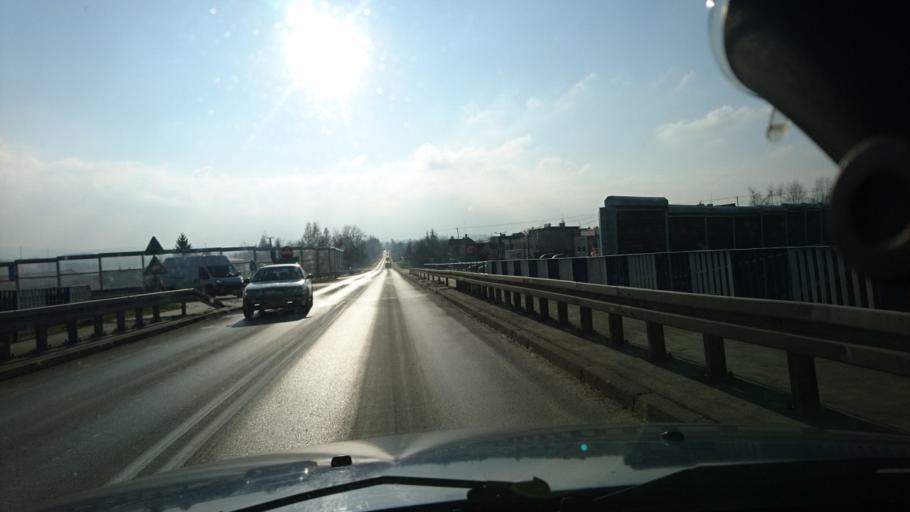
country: PL
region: Silesian Voivodeship
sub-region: Powiat cieszynski
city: Zamarski
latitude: 49.7632
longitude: 18.6821
